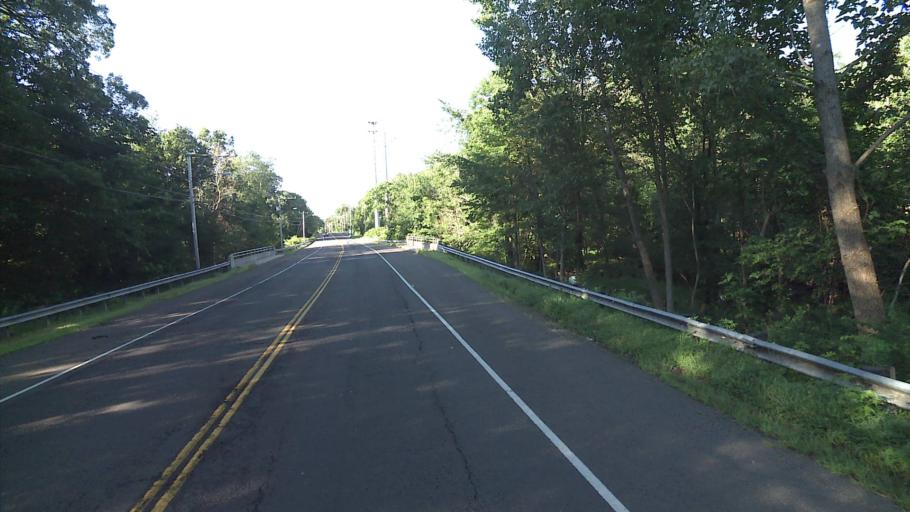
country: US
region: Connecticut
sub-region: New Haven County
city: Cheshire
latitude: 41.4495
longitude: -72.9098
